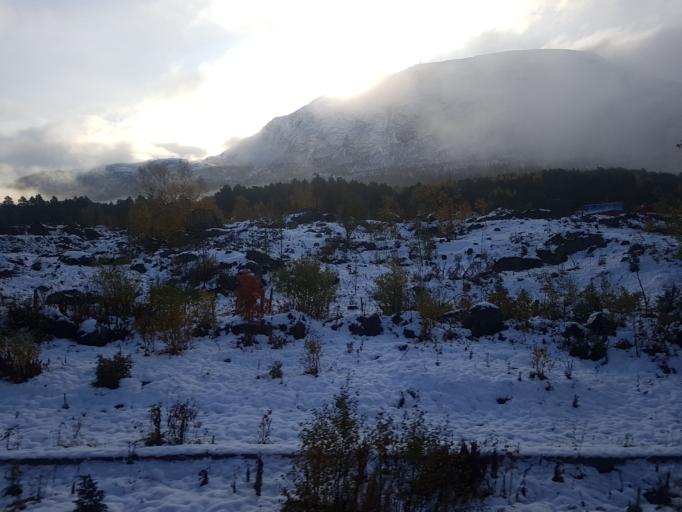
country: NO
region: Sor-Trondelag
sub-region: Oppdal
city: Oppdal
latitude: 62.5865
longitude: 9.6729
